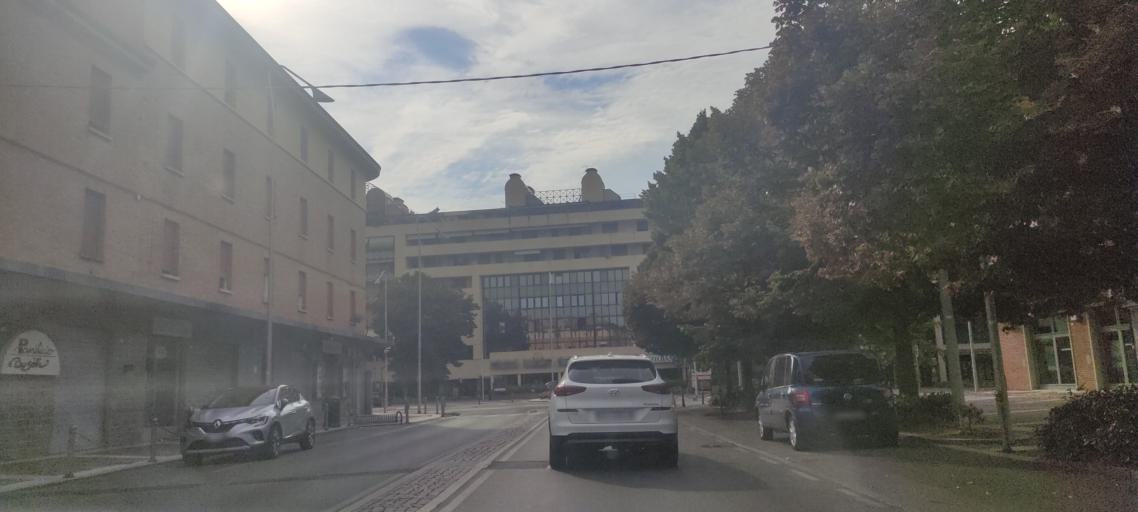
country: IT
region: Emilia-Romagna
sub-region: Provincia di Bologna
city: Castel Maggiore
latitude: 44.5750
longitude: 11.3644
